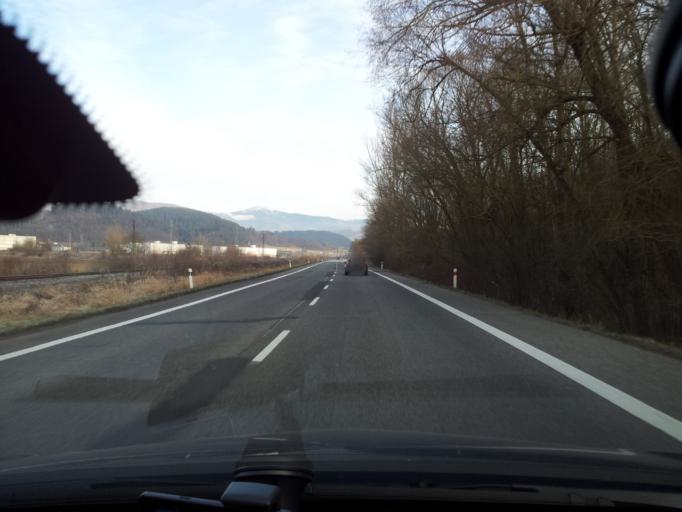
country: SK
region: Banskobystricky
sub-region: Okres Banska Bystrica
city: Banska Bystrica
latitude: 48.7484
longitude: 19.2530
